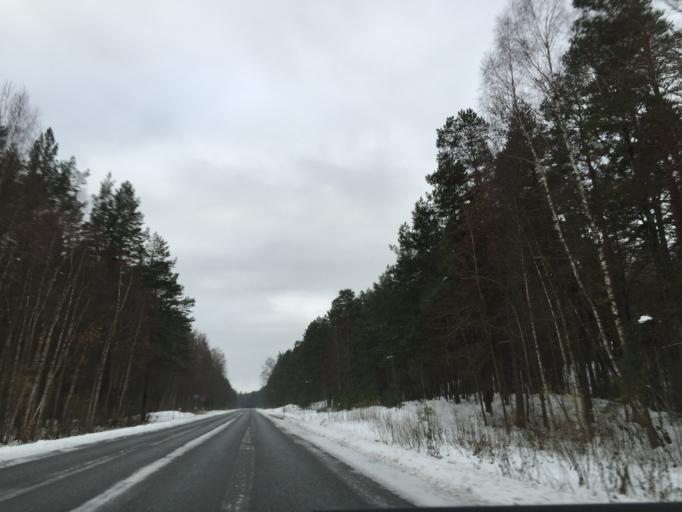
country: LV
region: Saulkrastu
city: Saulkrasti
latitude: 57.2220
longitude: 24.3888
